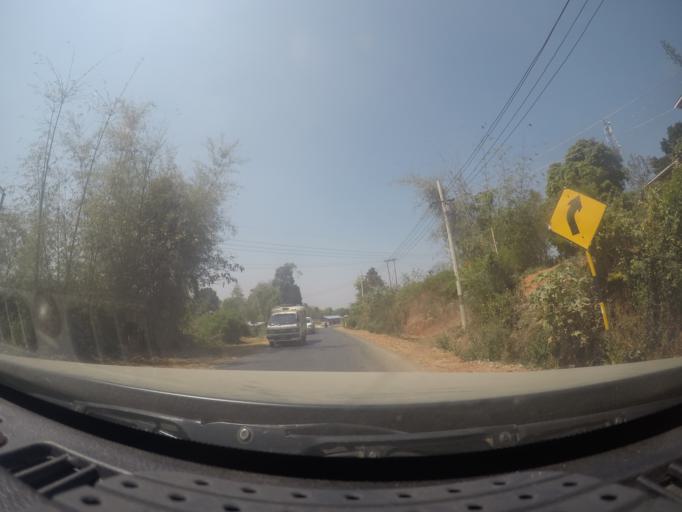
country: MM
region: Shan
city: Taunggyi
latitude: 20.9194
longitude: 96.5590
